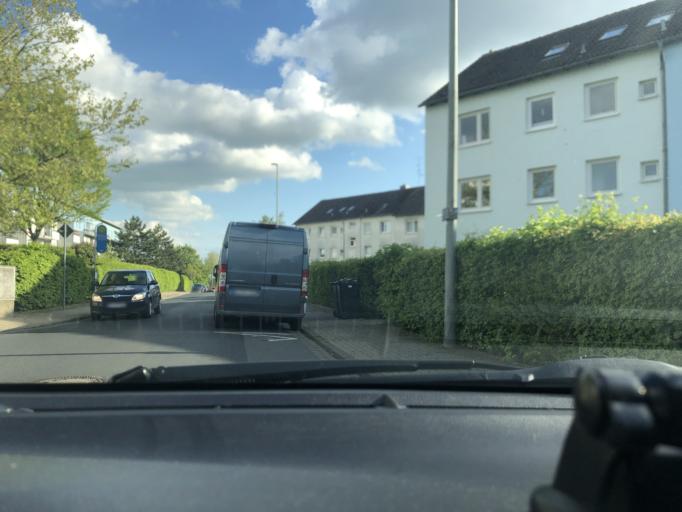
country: DE
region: Lower Saxony
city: Wolfenbuettel
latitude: 52.1759
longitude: 10.5581
